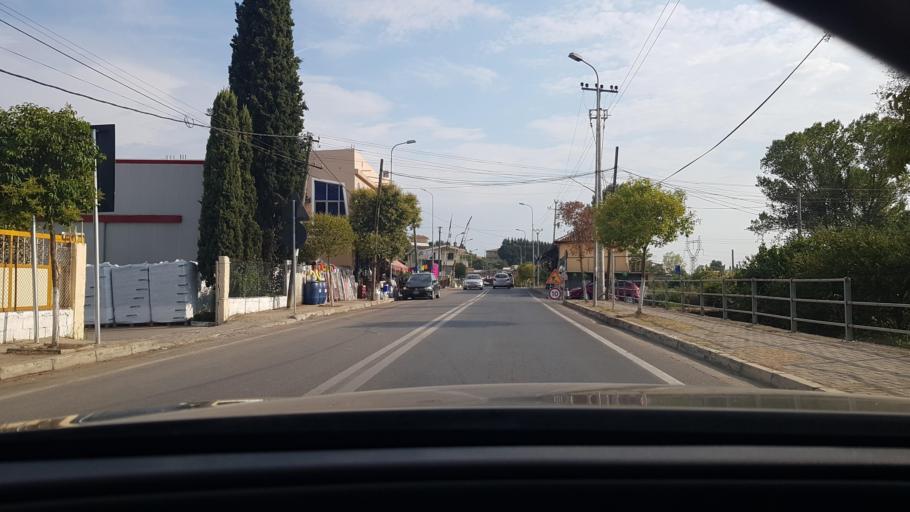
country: AL
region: Durres
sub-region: Rrethi i Durresit
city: Maminas
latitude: 41.3738
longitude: 19.6062
